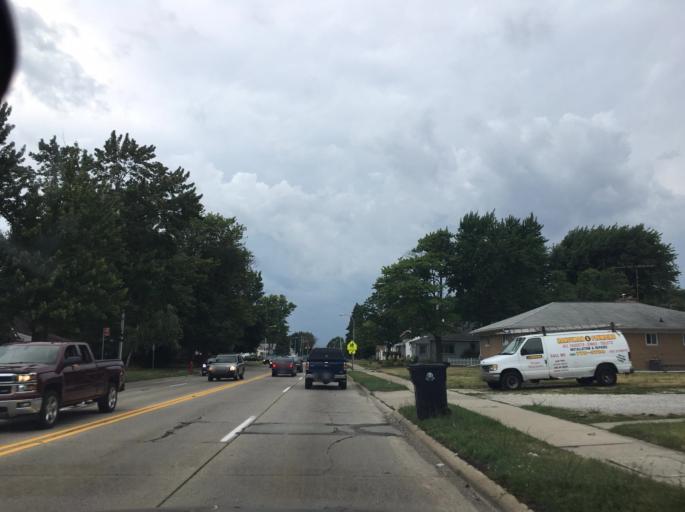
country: US
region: Michigan
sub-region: Macomb County
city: Roseville
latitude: 42.5098
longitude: -82.9317
